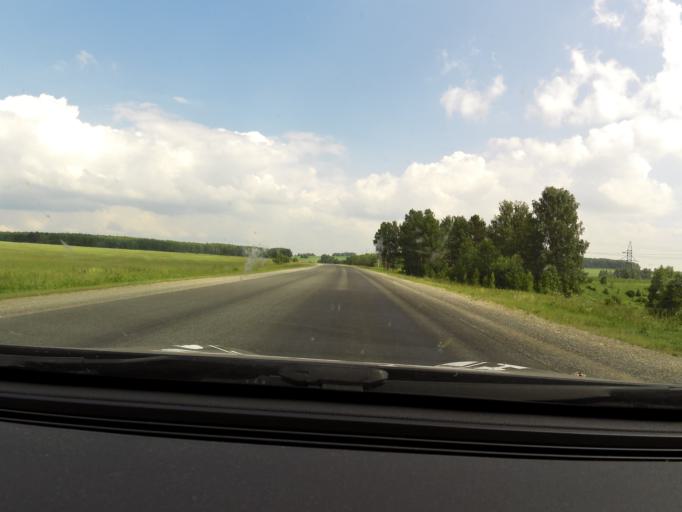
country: RU
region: Sverdlovsk
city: Ufimskiy
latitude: 56.7727
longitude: 58.0154
